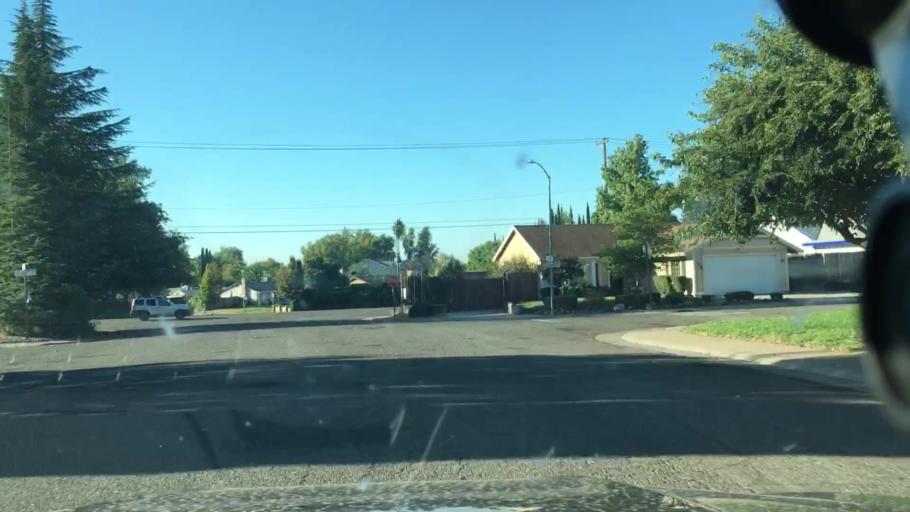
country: US
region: California
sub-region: Sacramento County
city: Antelope
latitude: 38.7044
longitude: -121.3421
